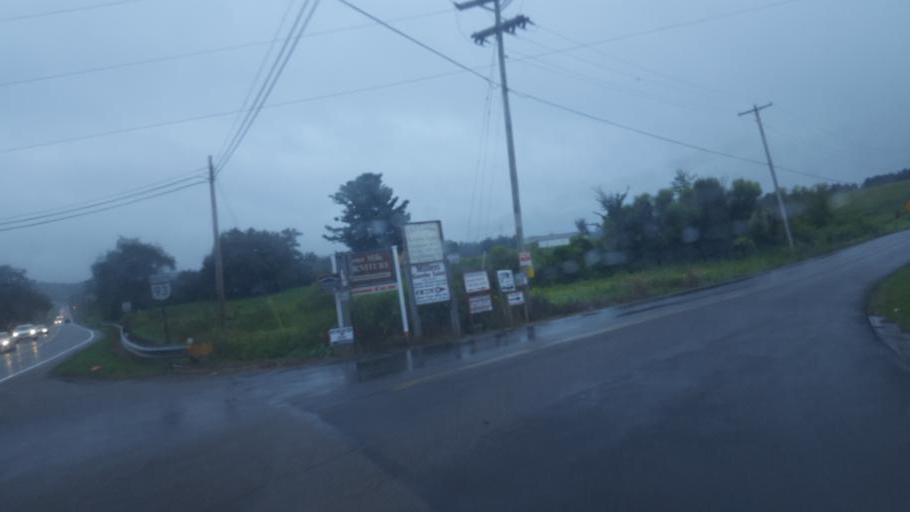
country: US
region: Ohio
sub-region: Jackson County
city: Jackson
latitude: 39.0238
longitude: -82.6188
